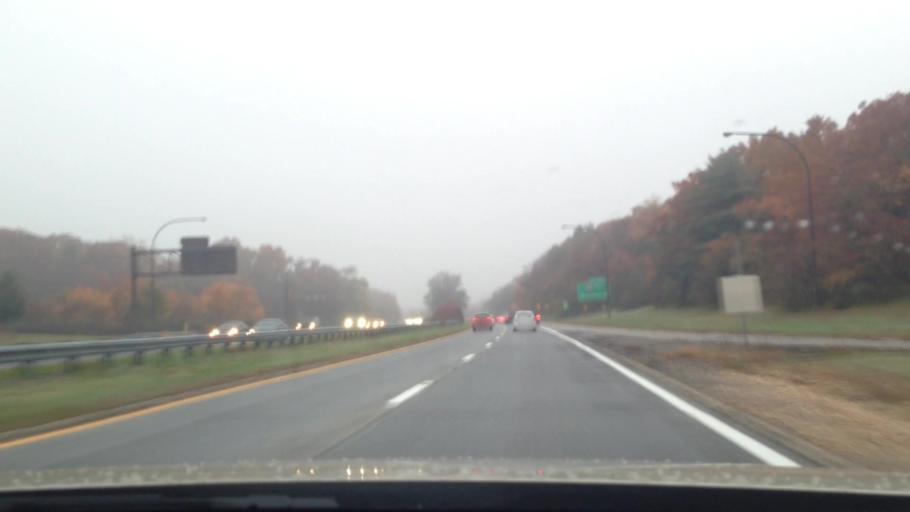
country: US
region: New York
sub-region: Suffolk County
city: Brentwood
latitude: 40.7986
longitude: -73.2789
